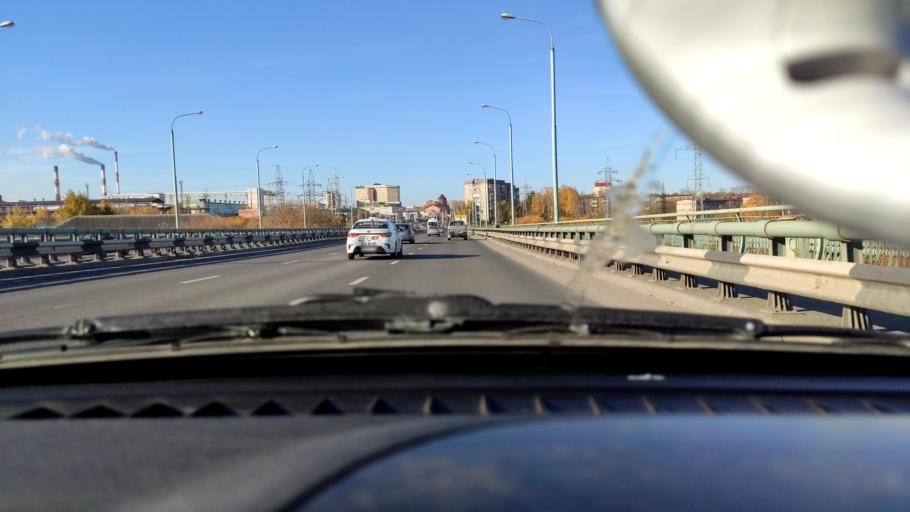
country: RU
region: Perm
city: Perm
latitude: 57.9873
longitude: 56.2792
